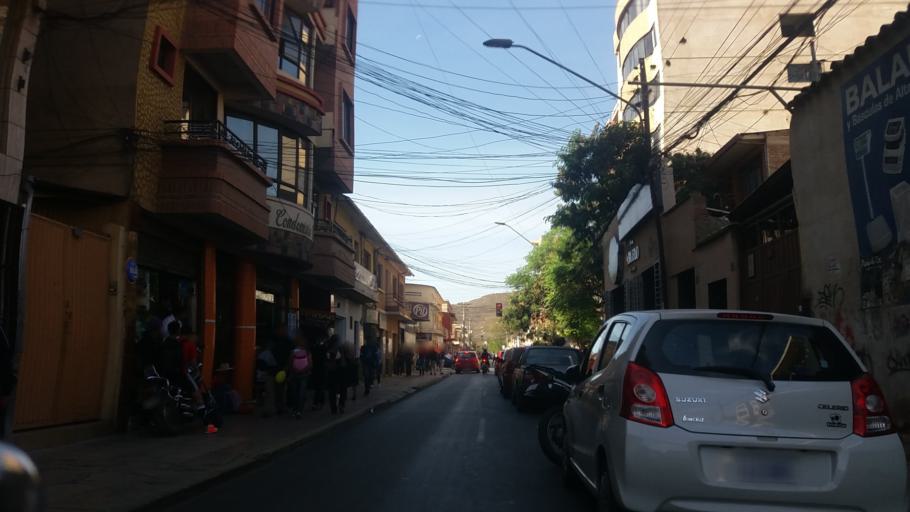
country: BO
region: Cochabamba
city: Cochabamba
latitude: -17.3934
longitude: -66.1515
